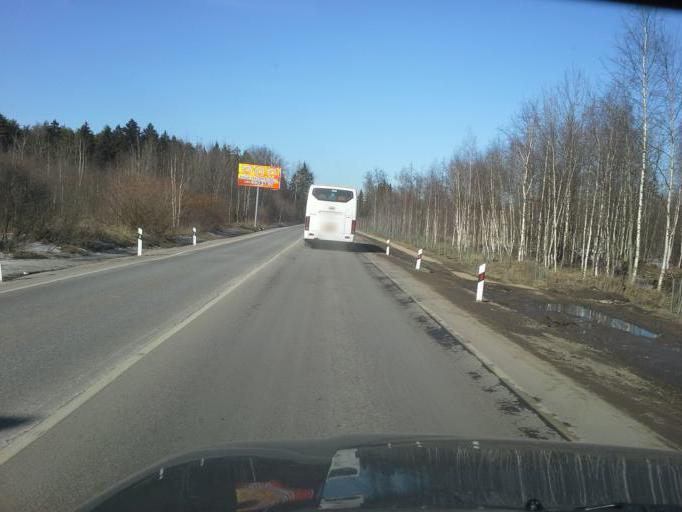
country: RU
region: Moskovskaya
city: Lesnoy Gorodok
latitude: 55.6638
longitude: 37.1801
